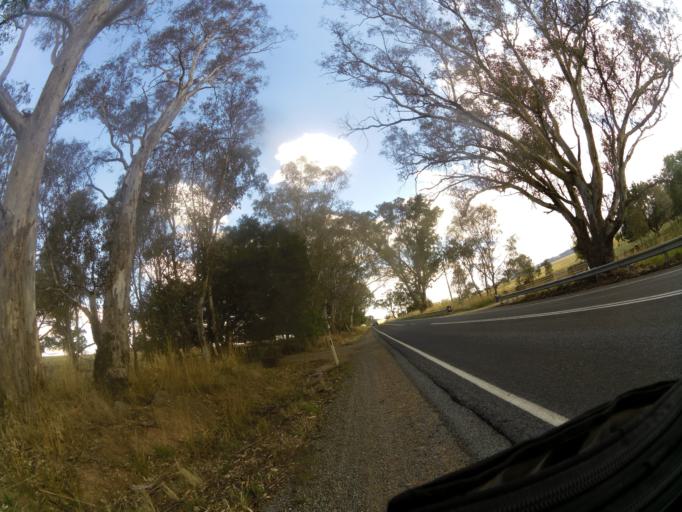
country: AU
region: Victoria
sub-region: Mansfield
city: Mansfield
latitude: -36.9394
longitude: 145.9987
